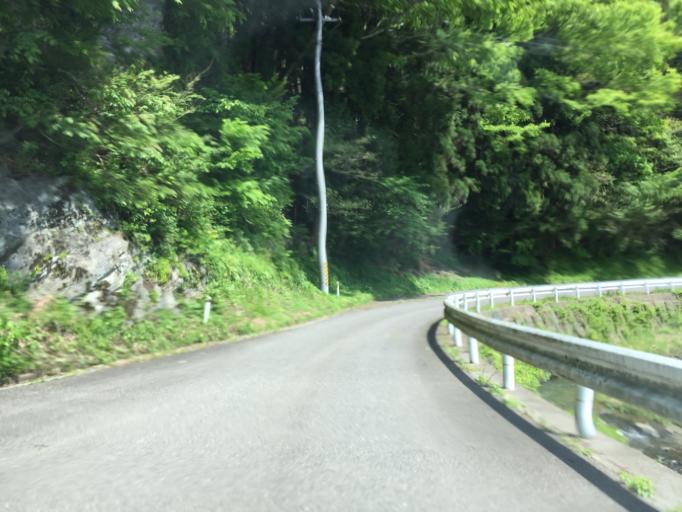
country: JP
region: Fukushima
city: Ishikawa
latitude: 37.1574
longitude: 140.5147
